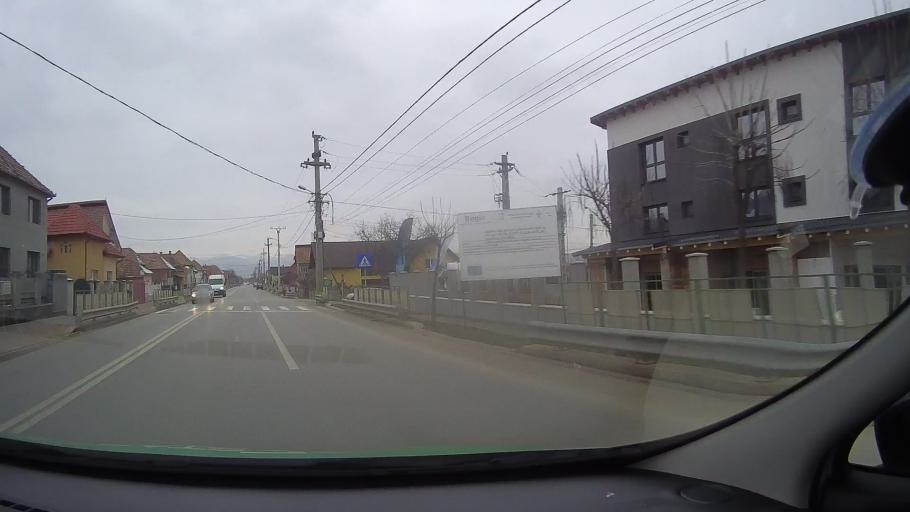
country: RO
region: Alba
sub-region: Municipiul Alba Iulia
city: Micesti
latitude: 46.1002
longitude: 23.5503
